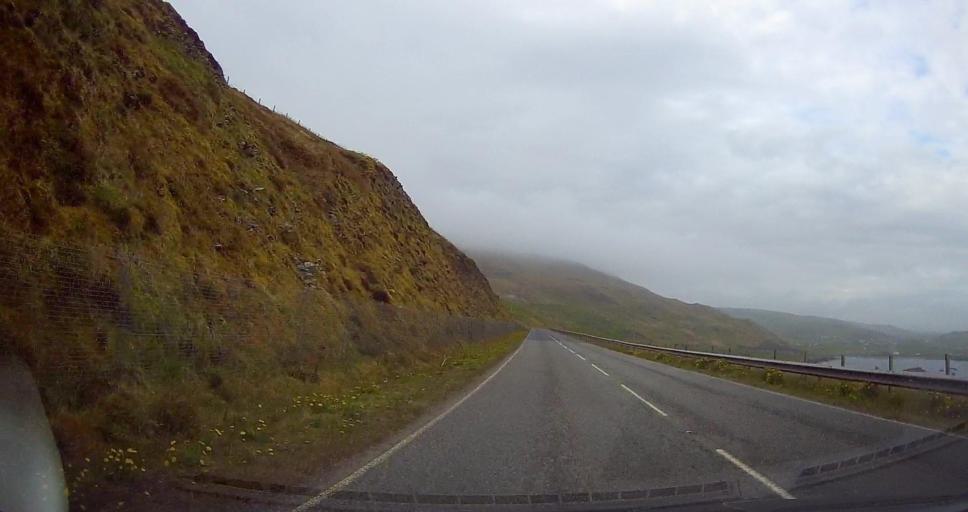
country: GB
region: Scotland
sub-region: Shetland Islands
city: Sandwick
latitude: 60.0198
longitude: -1.2318
